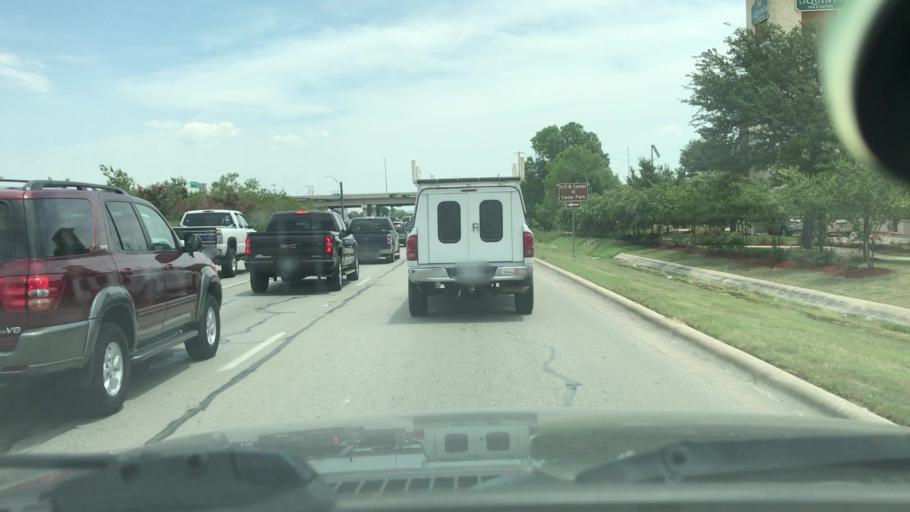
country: US
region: Texas
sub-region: Williamson County
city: Cedar Park
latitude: 30.5244
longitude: -97.8185
